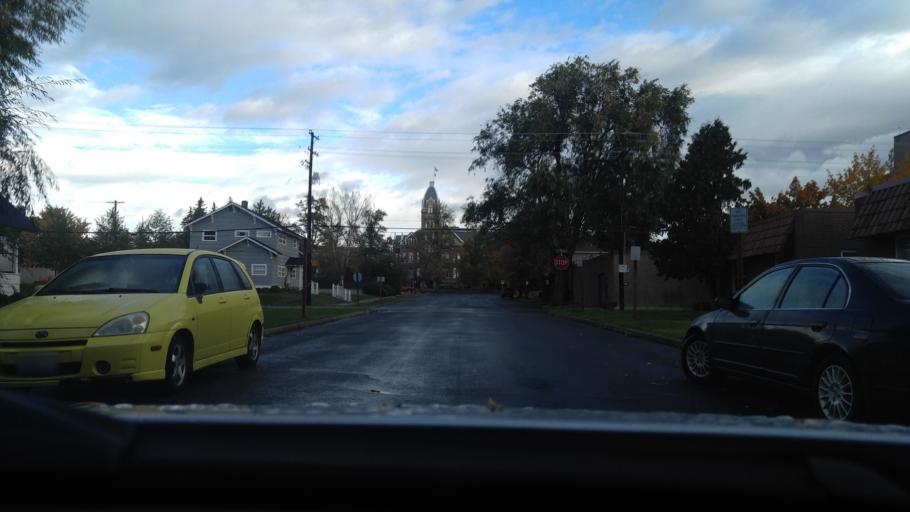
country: US
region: Washington
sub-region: Kittitas County
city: Ellensburg
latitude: 46.9983
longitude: -120.5420
